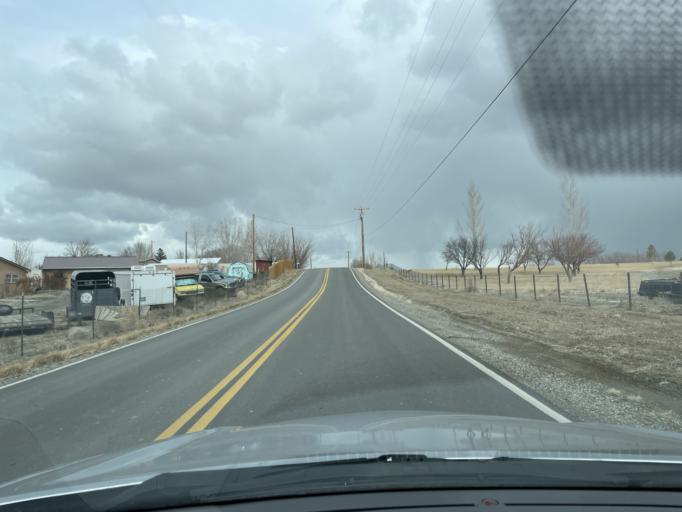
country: US
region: Colorado
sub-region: Mesa County
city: Loma
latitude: 39.1951
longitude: -108.8083
